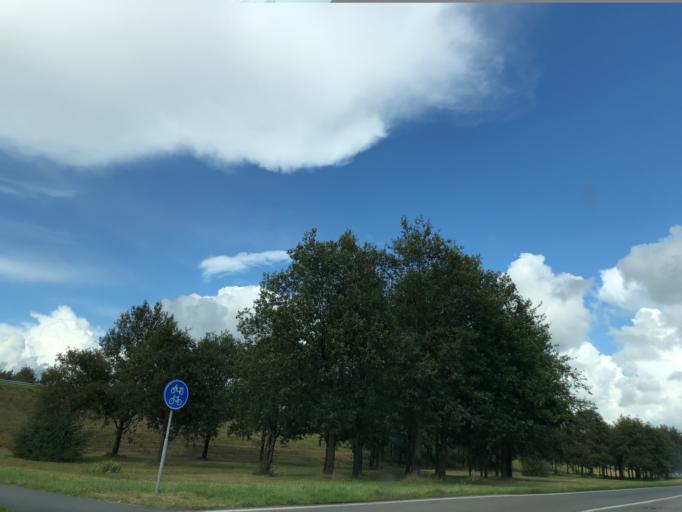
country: NL
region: Groningen
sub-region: Gemeente Grootegast
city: Grootegast
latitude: 53.1531
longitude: 6.2712
